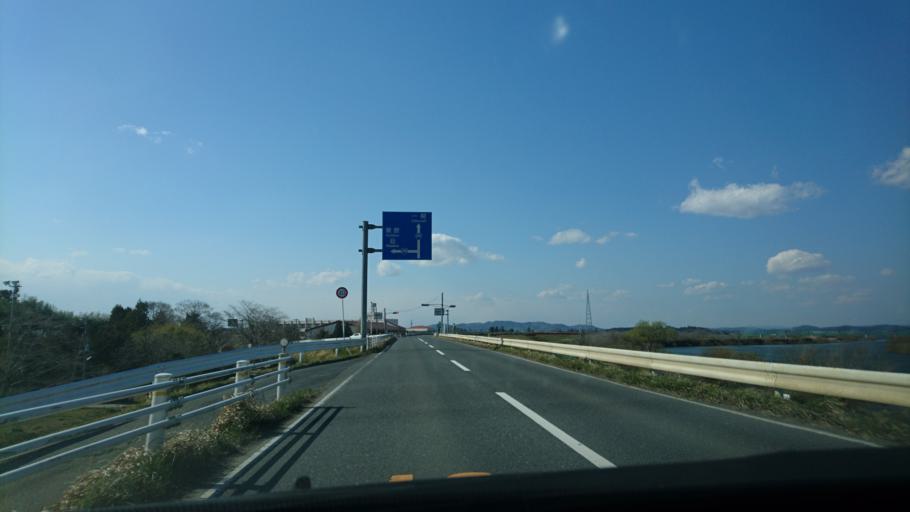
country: JP
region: Miyagi
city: Wakuya
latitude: 38.7069
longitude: 141.2686
